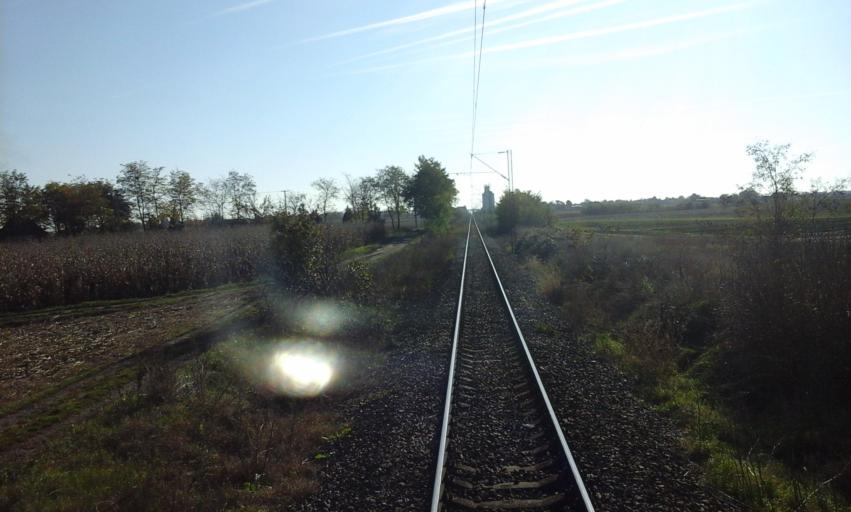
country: RS
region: Autonomna Pokrajina Vojvodina
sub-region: Severnobacki Okrug
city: Subotica
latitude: 45.9555
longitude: 19.6707
